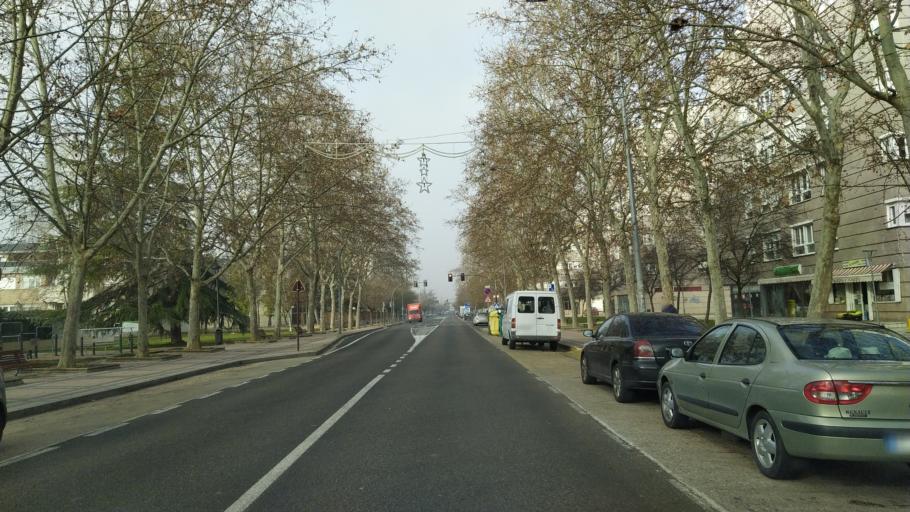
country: ES
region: Castille and Leon
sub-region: Provincia de Palencia
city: Palencia
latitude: 41.9951
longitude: -4.5174
